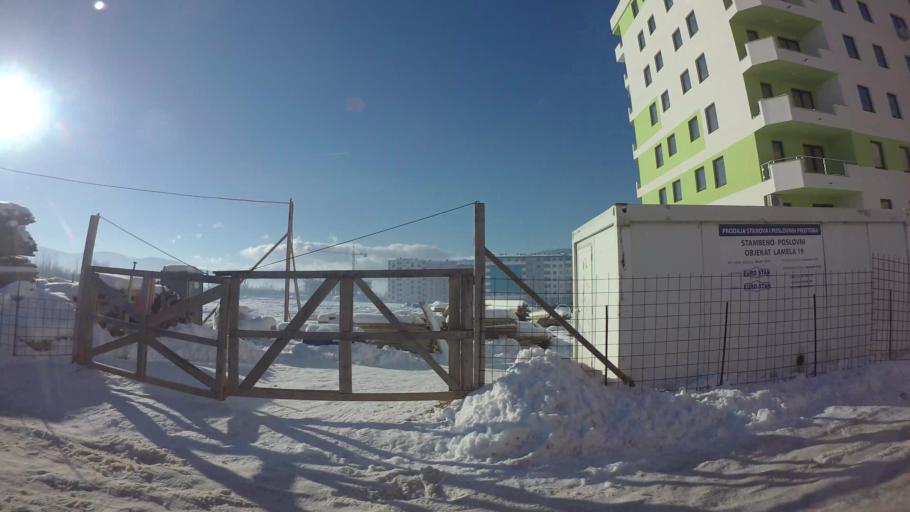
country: BA
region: Federation of Bosnia and Herzegovina
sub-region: Kanton Sarajevo
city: Sarajevo
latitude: 43.8196
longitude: 18.3654
